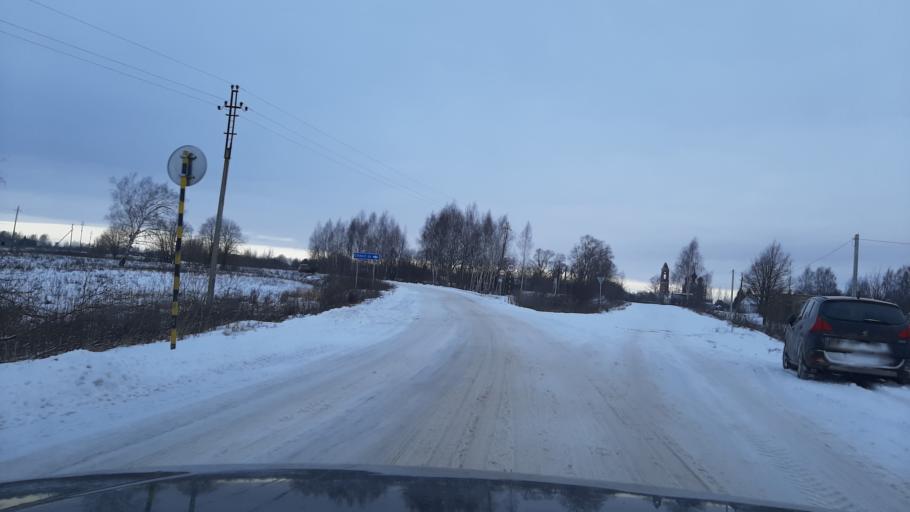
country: RU
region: Kostroma
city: Volgorechensk
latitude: 57.4482
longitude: 41.0303
